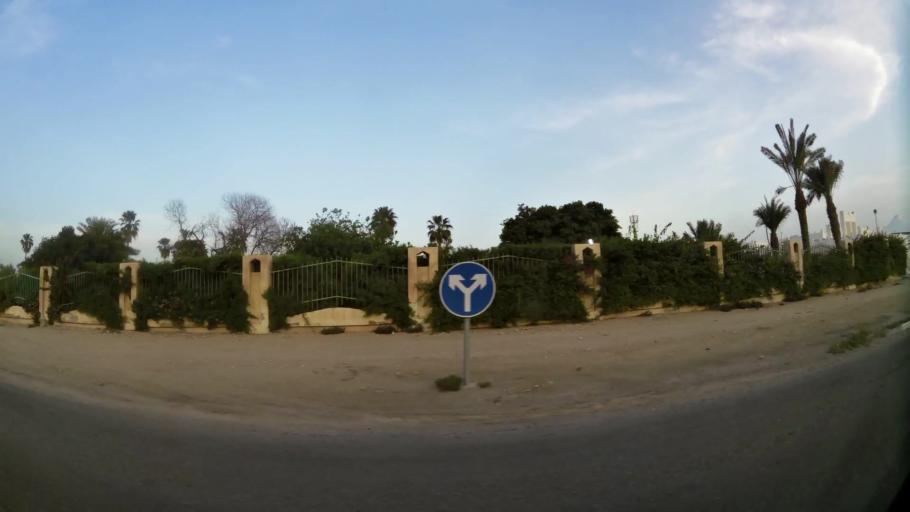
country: QA
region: Al Wakrah
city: Al Wakrah
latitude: 25.1794
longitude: 51.6106
